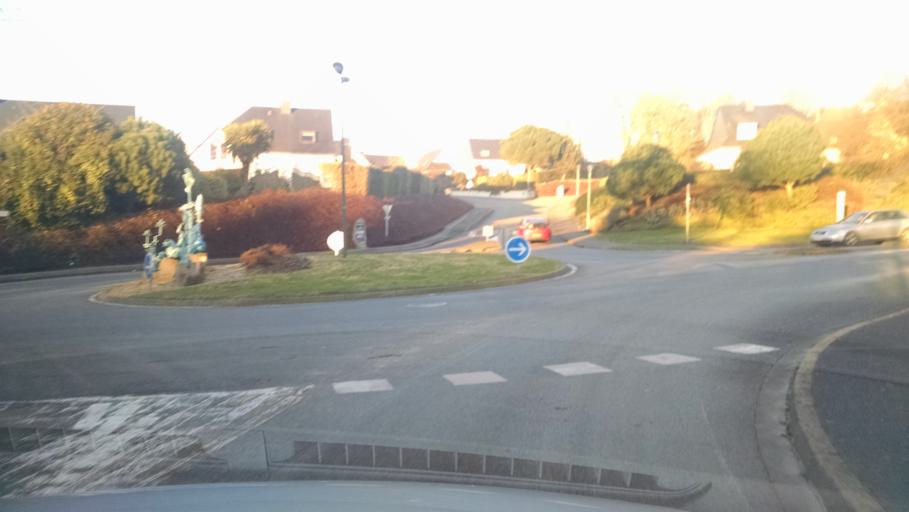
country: FR
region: Brittany
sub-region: Departement du Morbihan
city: Guidel-Plage
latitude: 47.7936
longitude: -3.5012
